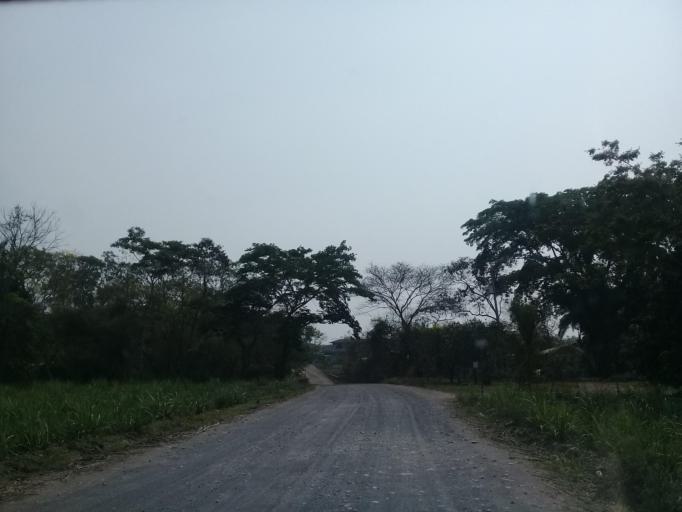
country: MX
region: Oaxaca
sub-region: Acatlan de Perez Figueroa
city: Zona Urbana Ejidal
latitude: 18.5879
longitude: -96.5623
